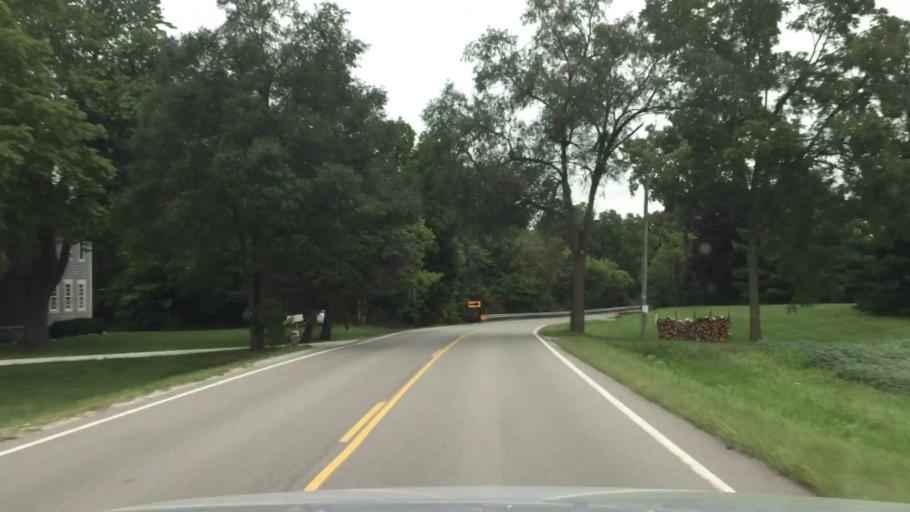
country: US
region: Michigan
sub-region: Washtenaw County
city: Milan
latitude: 42.0966
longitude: -83.7354
